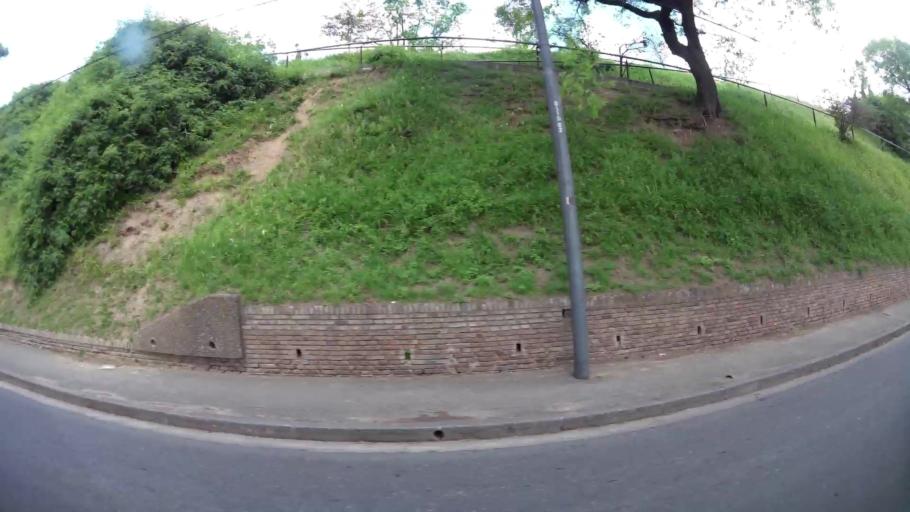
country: AR
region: Santa Fe
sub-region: Departamento de Rosario
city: Rosario
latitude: -32.9562
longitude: -60.6226
